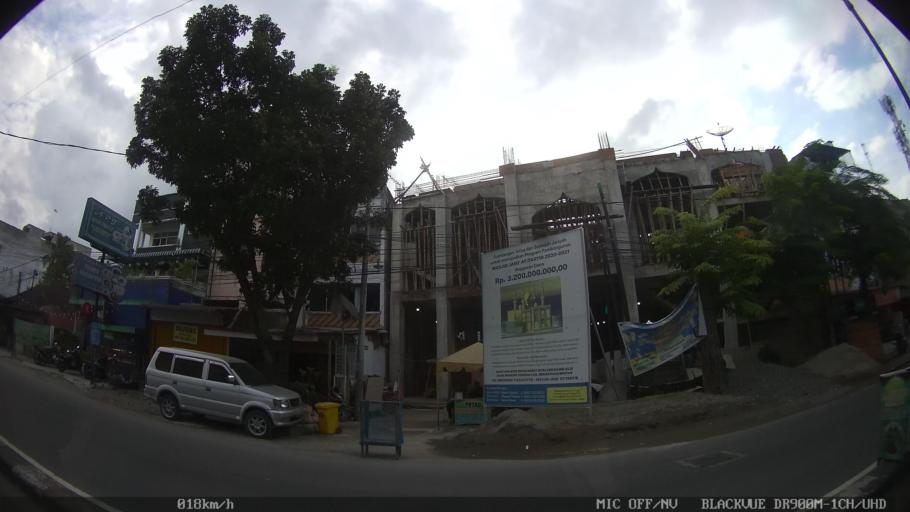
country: ID
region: North Sumatra
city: Medan
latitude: 3.6106
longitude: 98.6740
